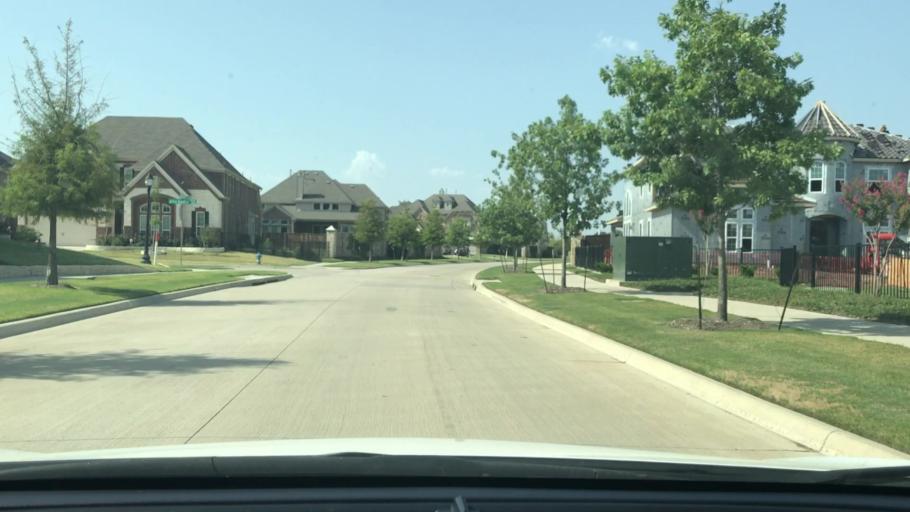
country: US
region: Texas
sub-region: Collin County
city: Frisco
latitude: 33.1271
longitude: -96.7652
